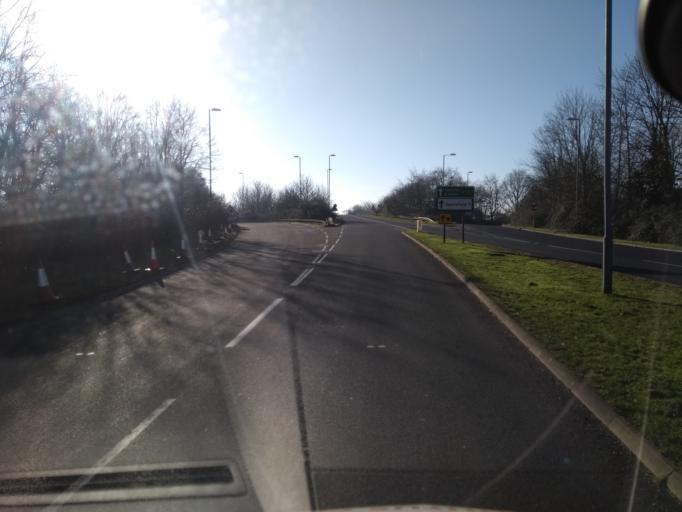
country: GB
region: England
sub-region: Somerset
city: Wincanton
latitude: 51.0499
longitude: -2.4185
